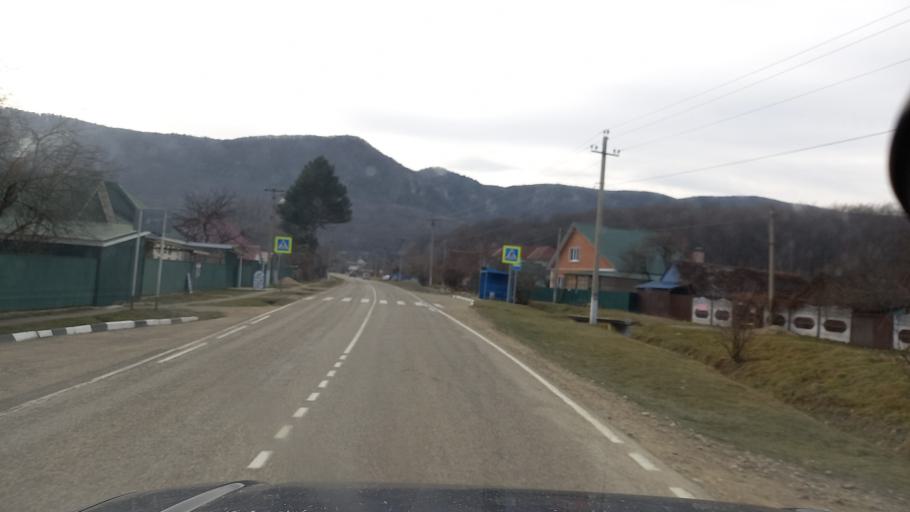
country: RU
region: Krasnodarskiy
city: Neftegorsk
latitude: 44.2352
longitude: 39.9028
